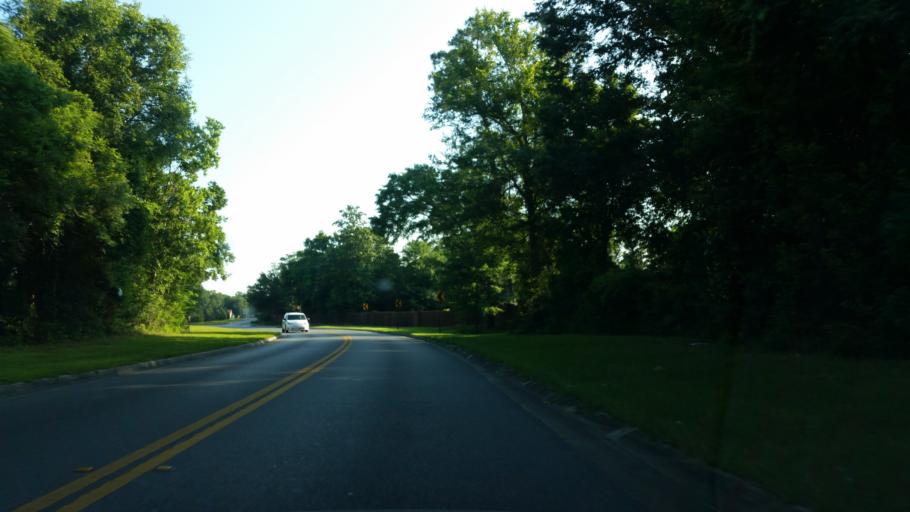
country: US
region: Florida
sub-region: Escambia County
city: Ferry Pass
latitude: 30.5135
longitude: -87.2376
